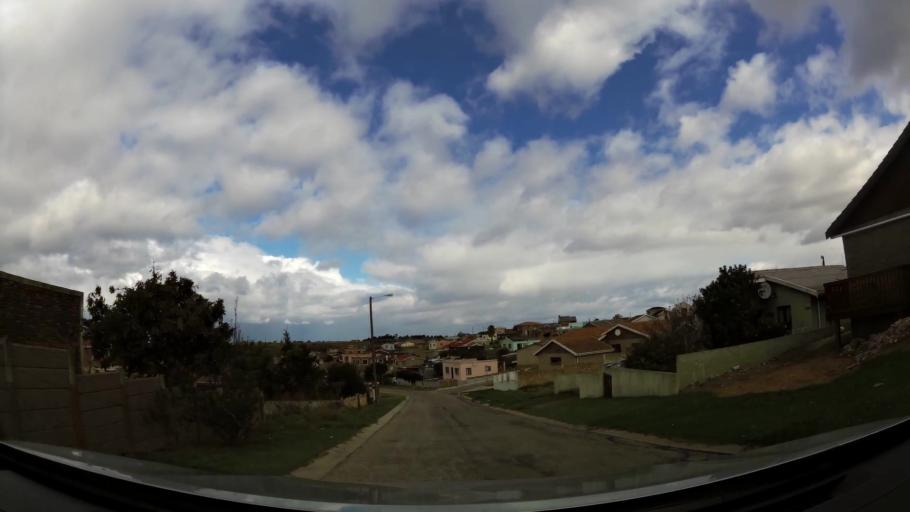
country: ZA
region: Western Cape
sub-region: Eden District Municipality
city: George
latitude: -34.0211
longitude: 22.4776
